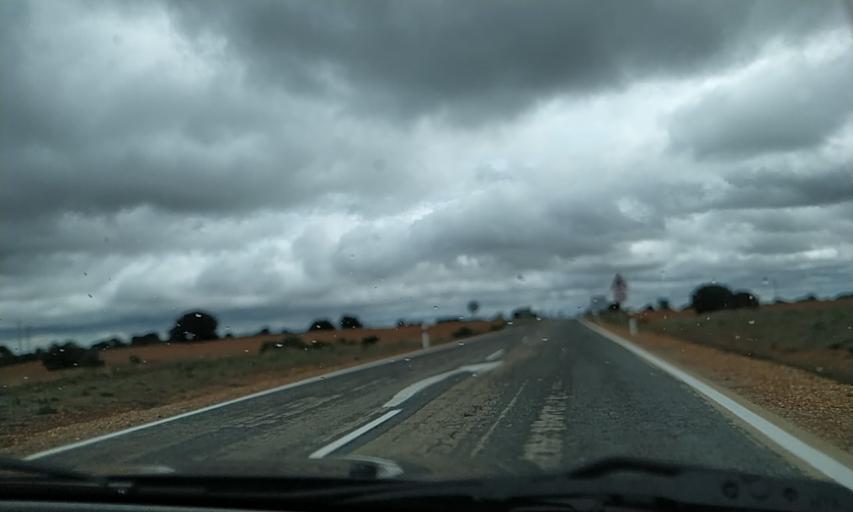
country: ES
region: Castille and Leon
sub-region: Provincia de Zamora
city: Perilla de Castro
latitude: 41.7379
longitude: -5.8305
